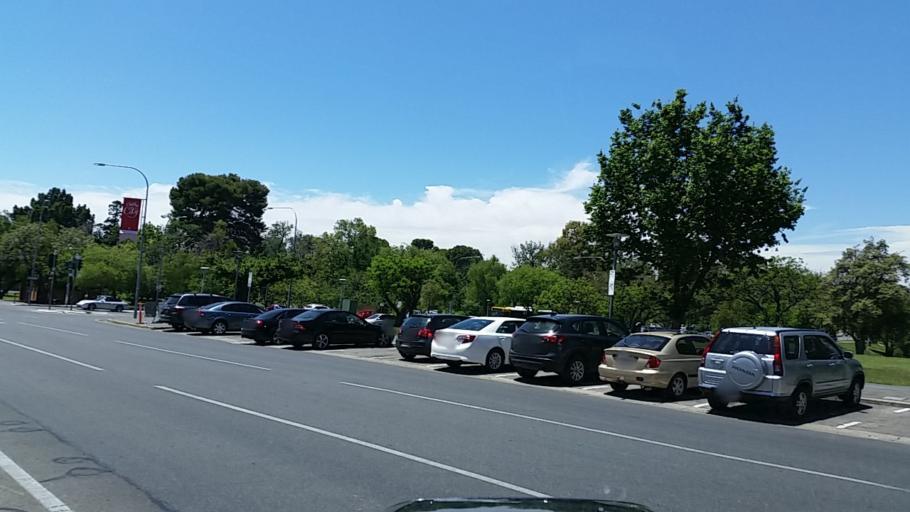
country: AU
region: South Australia
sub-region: Adelaide
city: Adelaide
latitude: -34.9231
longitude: 138.6109
